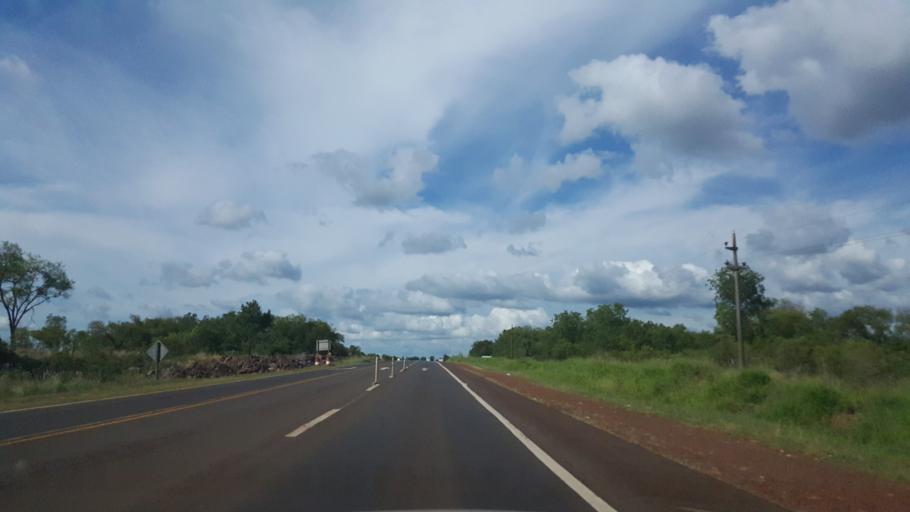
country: AR
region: Misiones
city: Santa Ana
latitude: -27.4175
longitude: -55.6128
